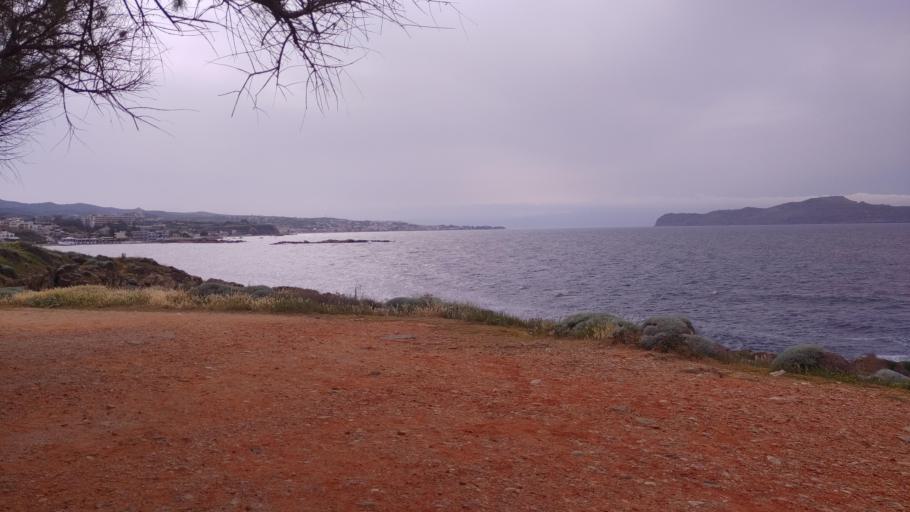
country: GR
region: Crete
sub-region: Nomos Chanias
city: Daratsos
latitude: 35.5158
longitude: 23.9778
